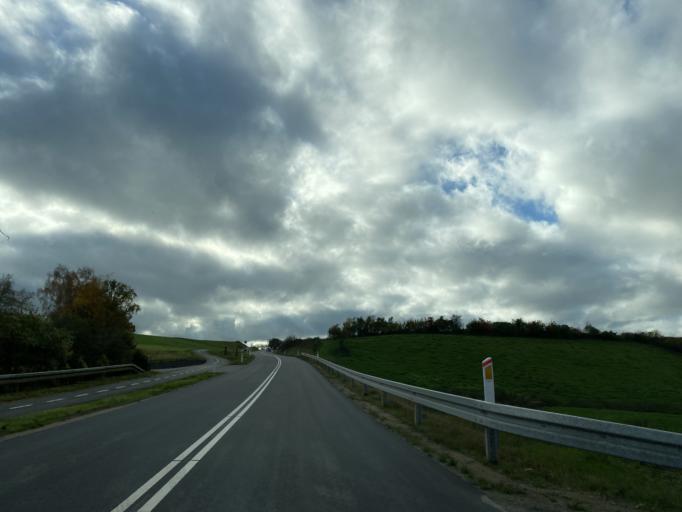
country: DK
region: Central Jutland
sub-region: Favrskov Kommune
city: Hammel
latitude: 56.2512
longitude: 9.8284
